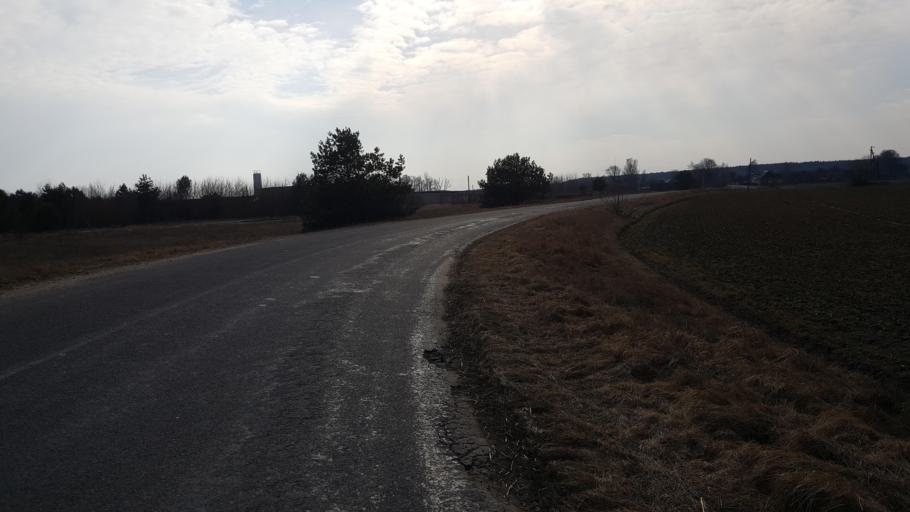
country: BY
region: Brest
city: Kamyanyets
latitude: 52.4088
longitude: 23.8921
